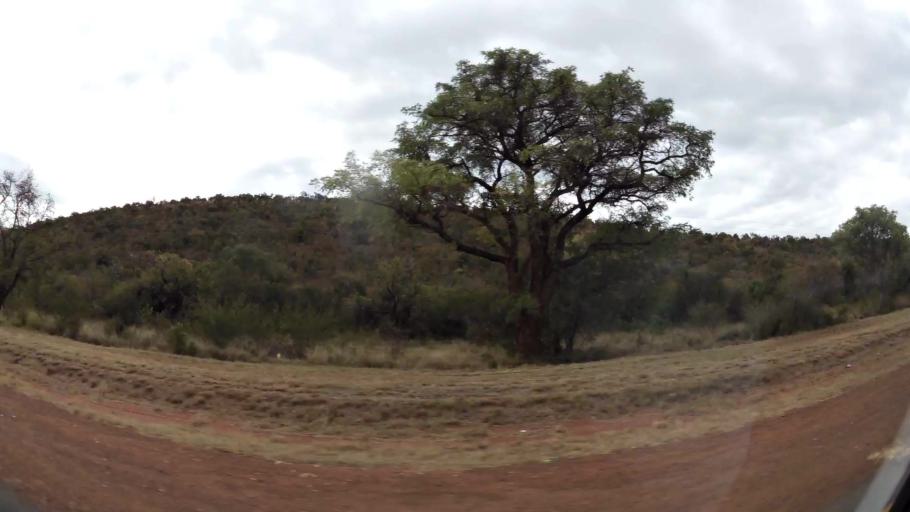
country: ZA
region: Limpopo
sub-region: Waterberg District Municipality
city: Modimolle
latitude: -24.6802
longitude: 28.5427
